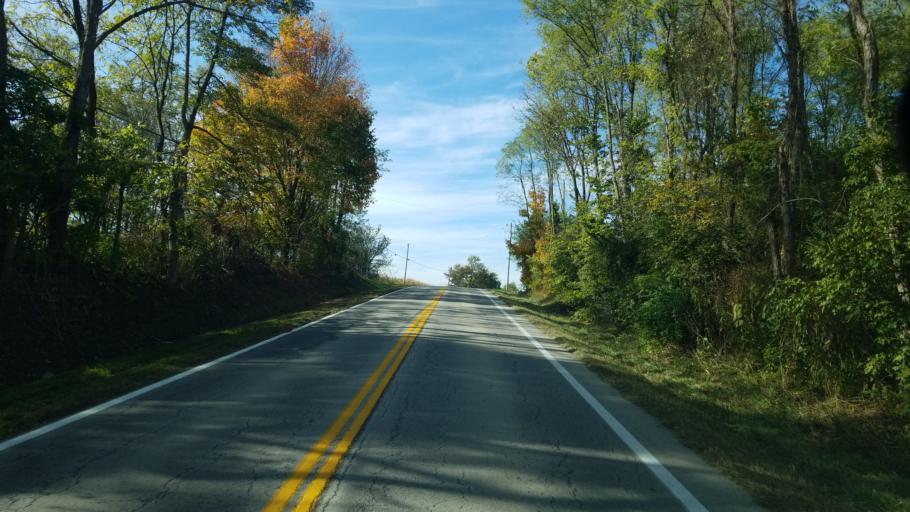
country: US
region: Ohio
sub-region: Clinton County
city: Blanchester
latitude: 39.3807
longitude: -83.9601
